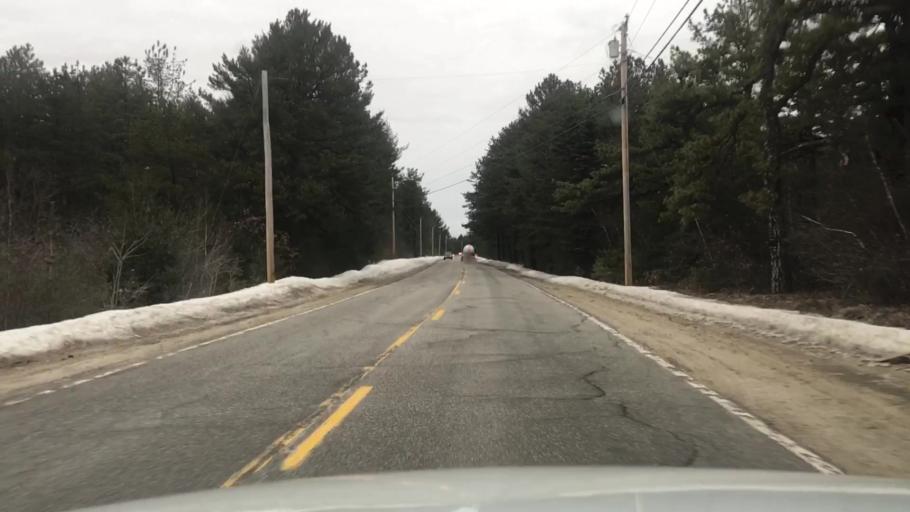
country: US
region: Maine
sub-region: York County
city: Shapleigh
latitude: 43.5682
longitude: -70.8597
